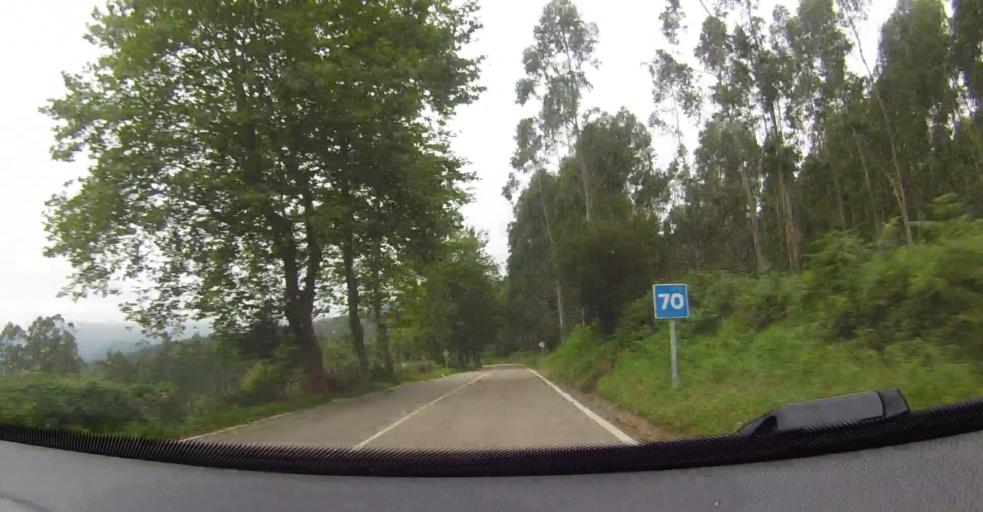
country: ES
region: Basque Country
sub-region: Bizkaia
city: Balmaseda
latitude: 43.2372
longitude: -3.2932
